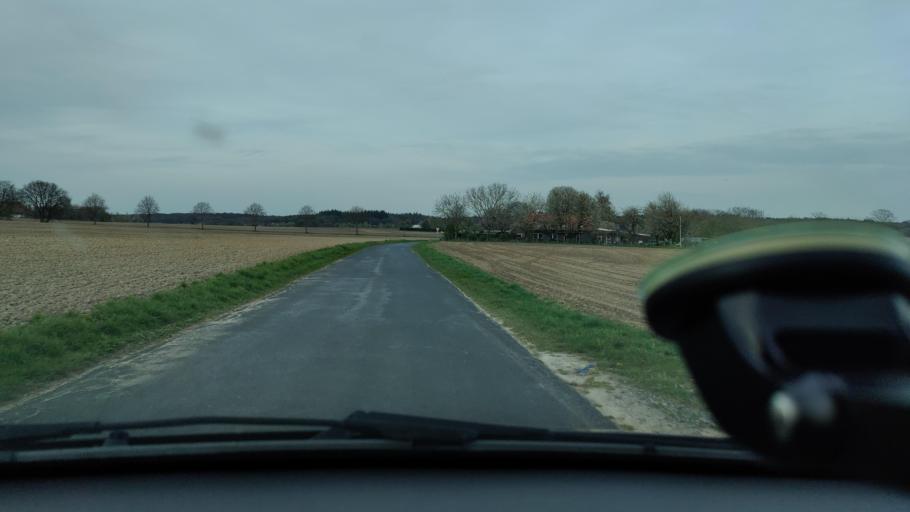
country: DE
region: North Rhine-Westphalia
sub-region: Regierungsbezirk Dusseldorf
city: Goch
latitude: 51.7418
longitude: 6.2053
